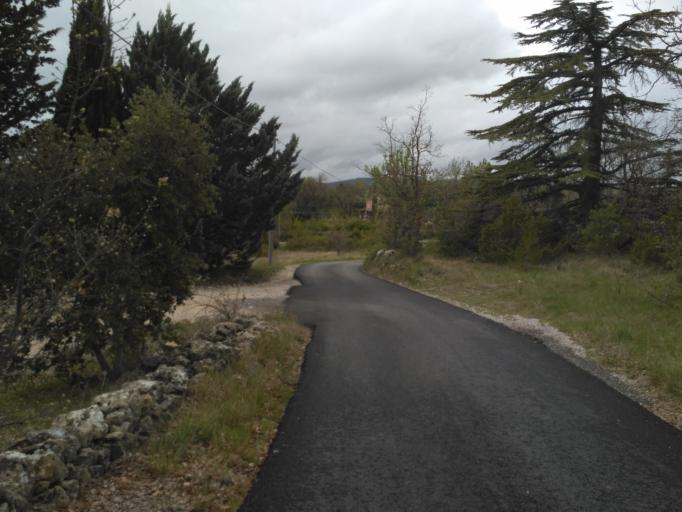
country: FR
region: Provence-Alpes-Cote d'Azur
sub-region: Departement du Var
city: Saint-Julien
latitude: 43.6355
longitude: 5.9179
